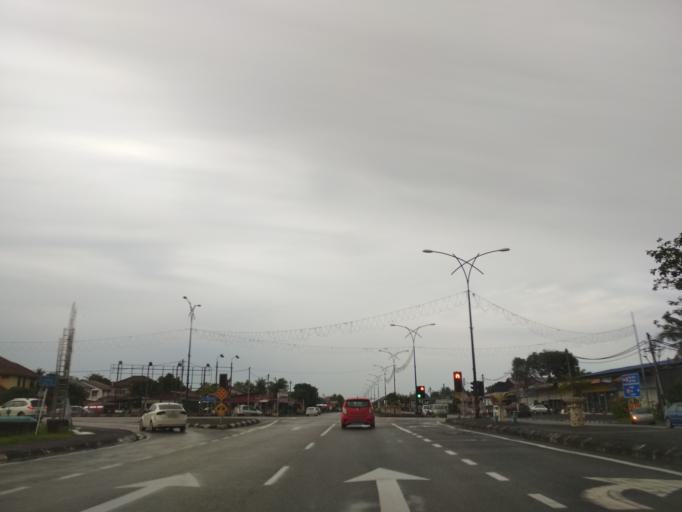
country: MY
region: Perlis
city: Kangar
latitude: 6.4534
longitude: 100.2063
